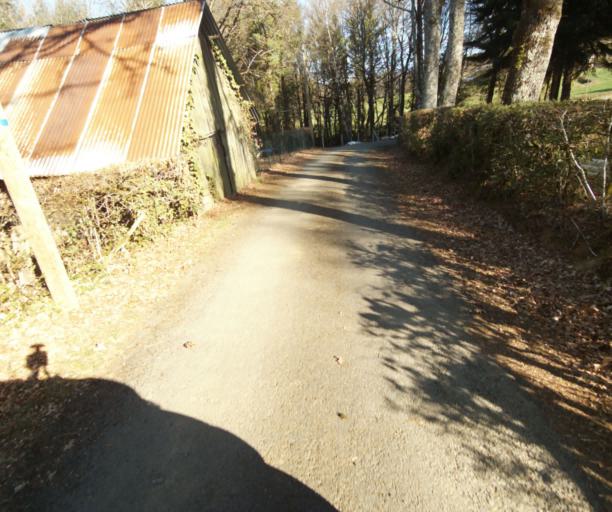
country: FR
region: Limousin
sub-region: Departement de la Correze
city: Seilhac
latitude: 45.3947
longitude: 1.7612
